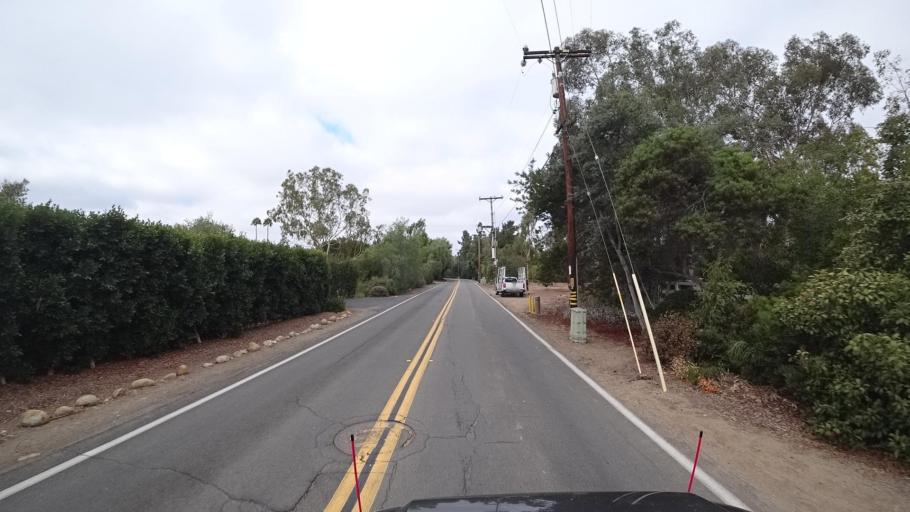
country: US
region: California
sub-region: San Diego County
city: Rancho Santa Fe
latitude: 33.0372
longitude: -117.2138
